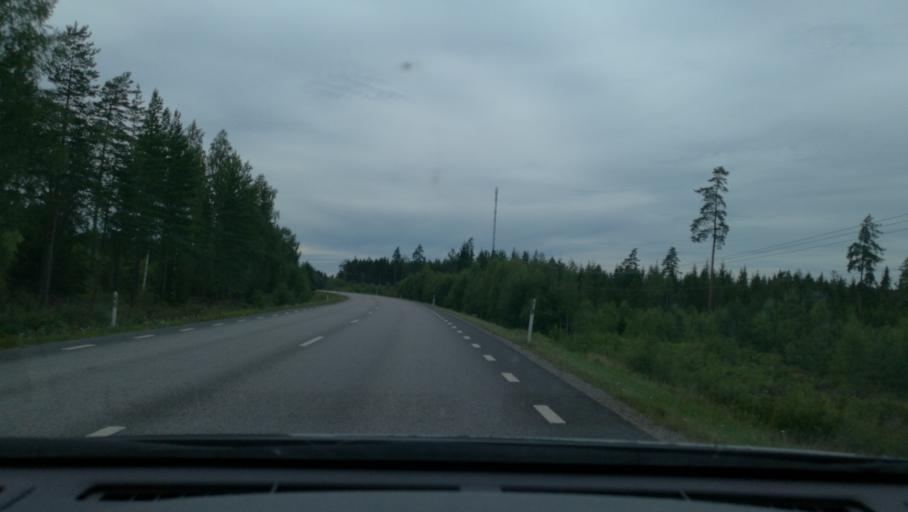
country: SE
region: Soedermanland
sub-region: Katrineholms Kommun
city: Katrineholm
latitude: 59.0814
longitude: 16.2052
